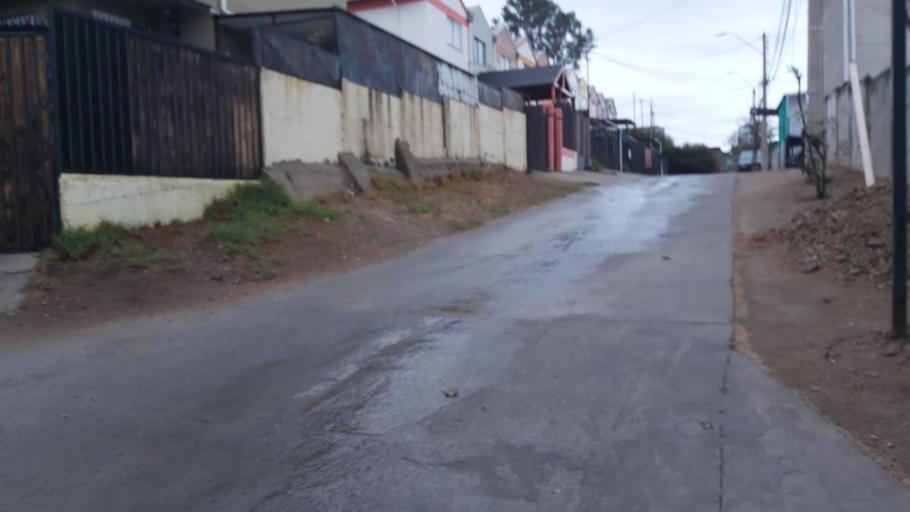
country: CL
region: Valparaiso
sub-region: Provincia de Marga Marga
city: Quilpue
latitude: -33.0527
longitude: -71.4210
